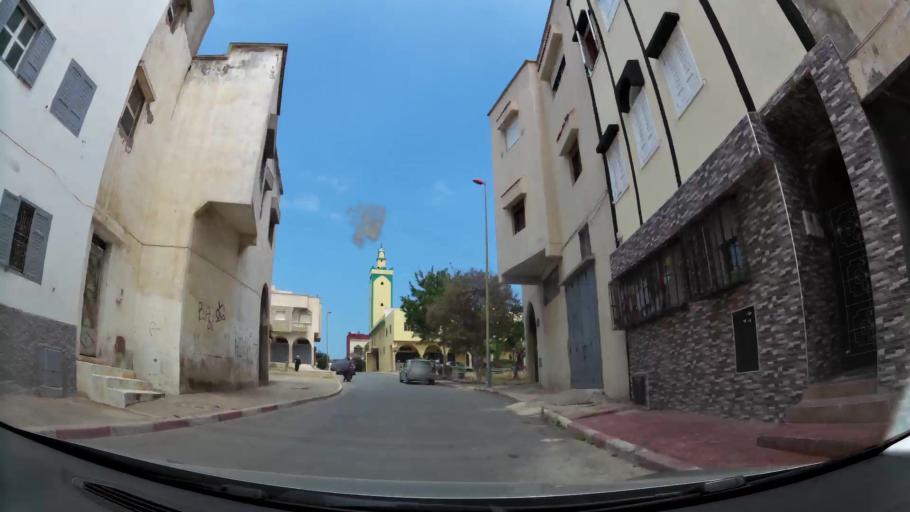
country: MA
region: Rabat-Sale-Zemmour-Zaer
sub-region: Skhirate-Temara
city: Temara
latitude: 33.9858
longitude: -6.8875
